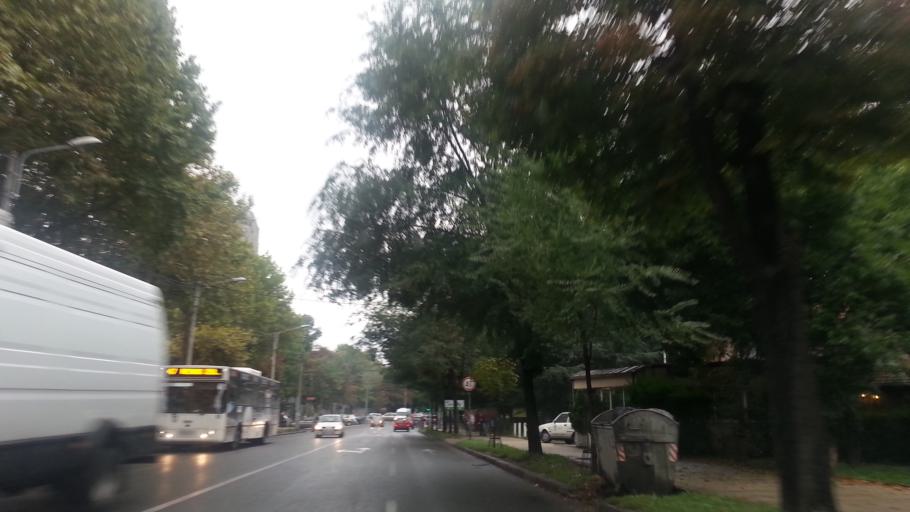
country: RS
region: Central Serbia
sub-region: Belgrade
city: Vozdovac
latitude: 44.7610
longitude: 20.4774
